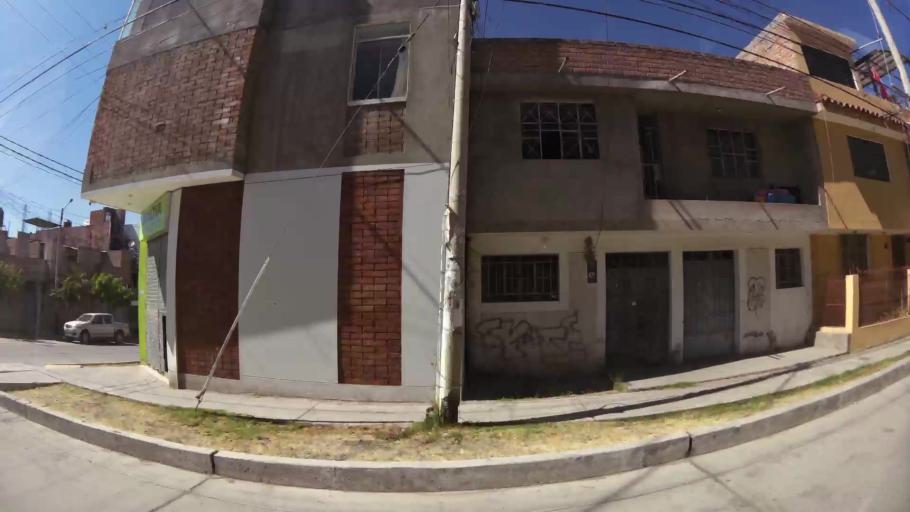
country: PE
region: Ayacucho
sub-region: Provincia de Huamanga
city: Ayacucho
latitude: -13.1465
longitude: -74.2273
